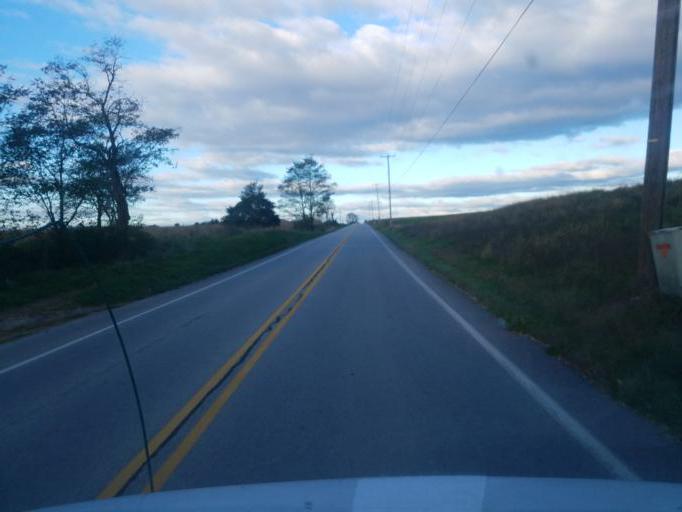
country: US
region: Pennsylvania
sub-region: Adams County
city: East Berlin
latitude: 39.9379
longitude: -77.0151
